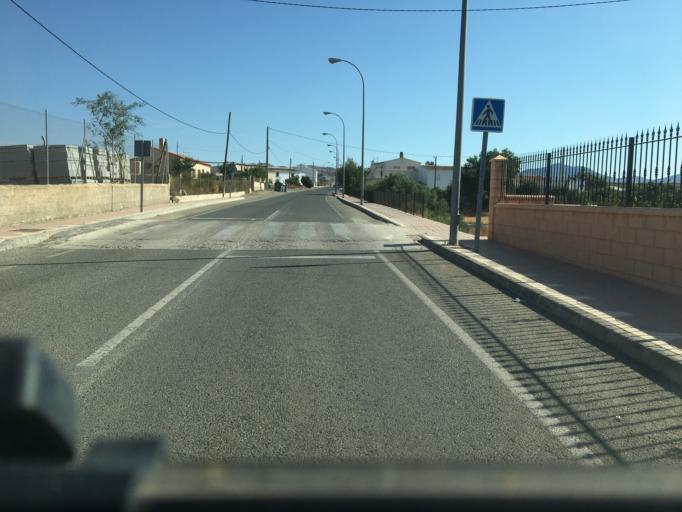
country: ES
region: Andalusia
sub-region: Provincia de Almeria
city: Huercal-Overa
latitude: 37.4643
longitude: -1.9877
